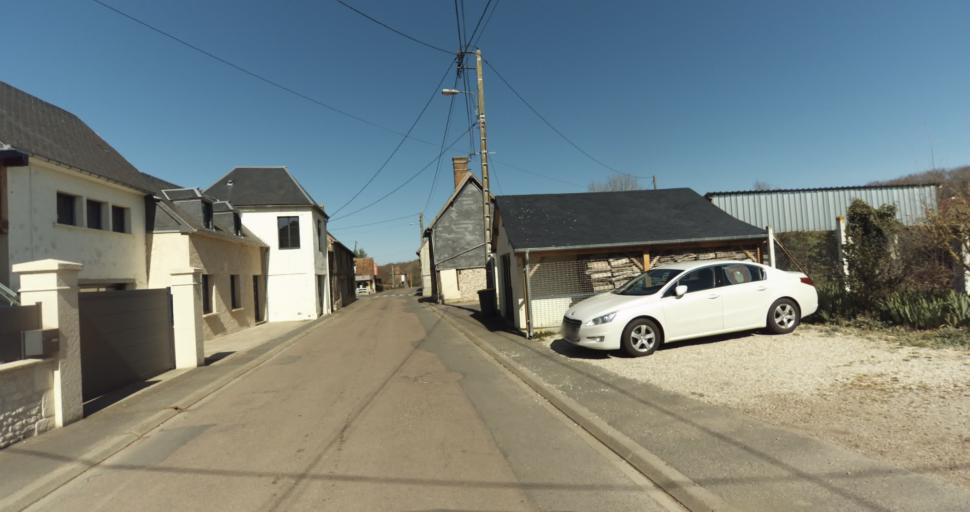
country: FR
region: Lower Normandy
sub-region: Departement du Calvados
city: Livarot
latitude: 48.9672
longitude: 0.0751
